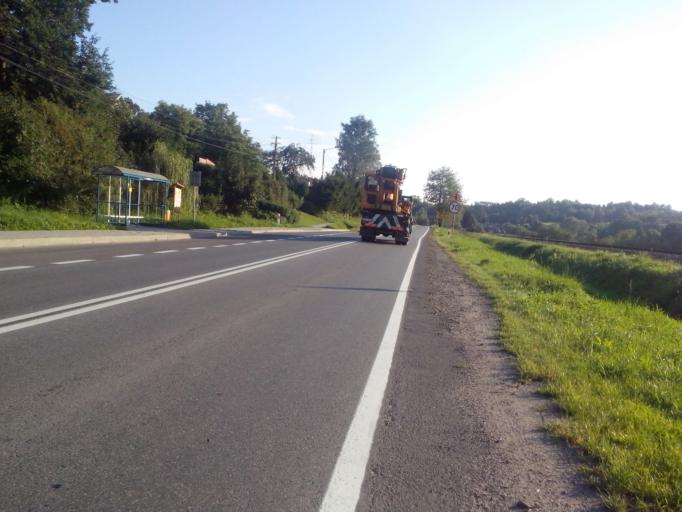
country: PL
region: Subcarpathian Voivodeship
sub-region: Powiat strzyzowski
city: Strzyzow
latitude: 49.8783
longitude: 21.8199
